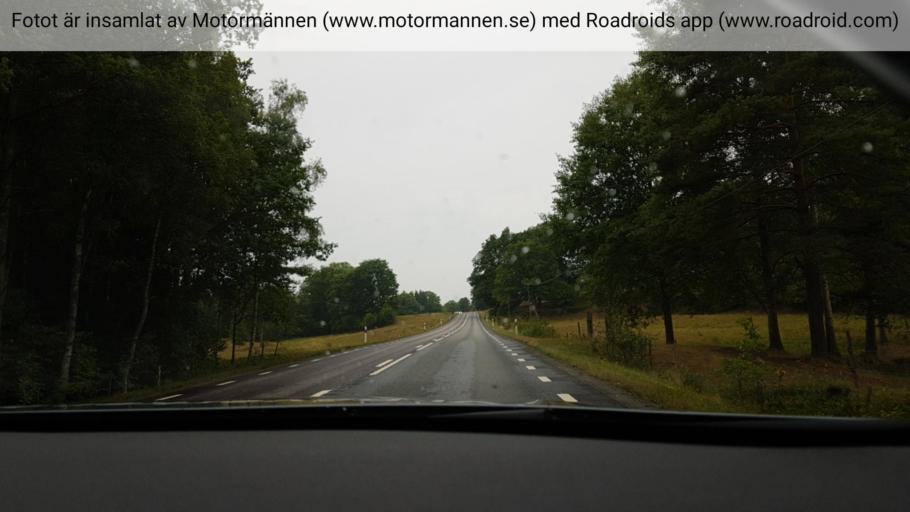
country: SE
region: Joenkoeping
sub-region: Varnamo Kommun
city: Varnamo
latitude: 57.2238
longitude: 14.1170
